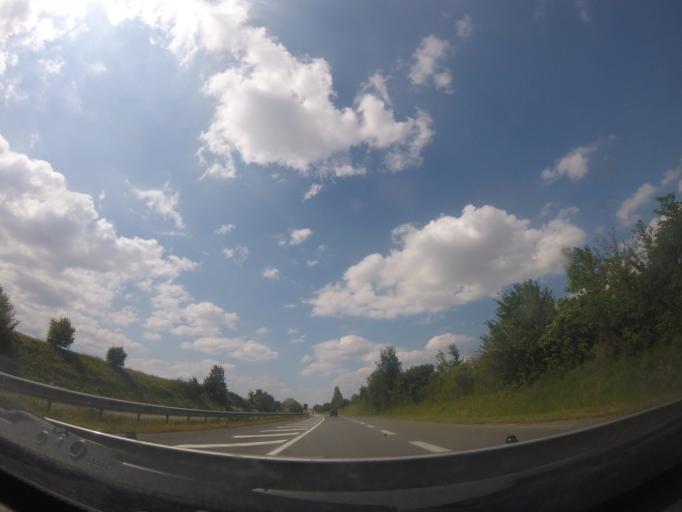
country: FR
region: Poitou-Charentes
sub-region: Departement de la Charente-Maritime
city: Saint-Porchaire
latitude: 45.8294
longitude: -0.7977
